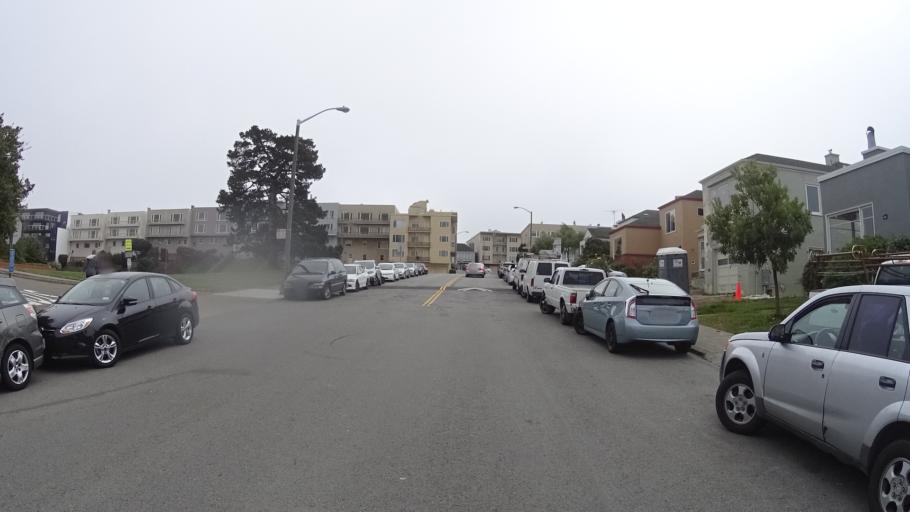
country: US
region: California
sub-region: San Francisco County
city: San Francisco
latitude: 37.7855
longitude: -122.4494
